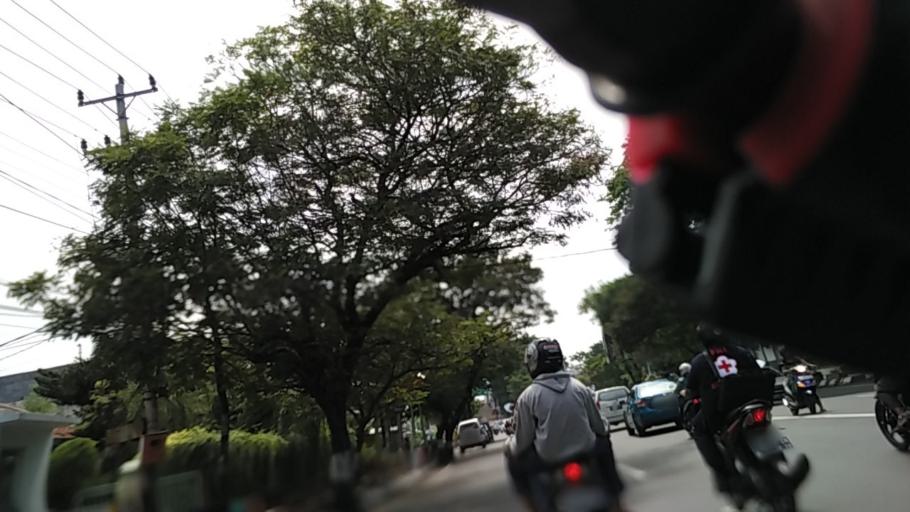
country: ID
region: Central Java
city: Semarang
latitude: -6.9936
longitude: 110.4302
